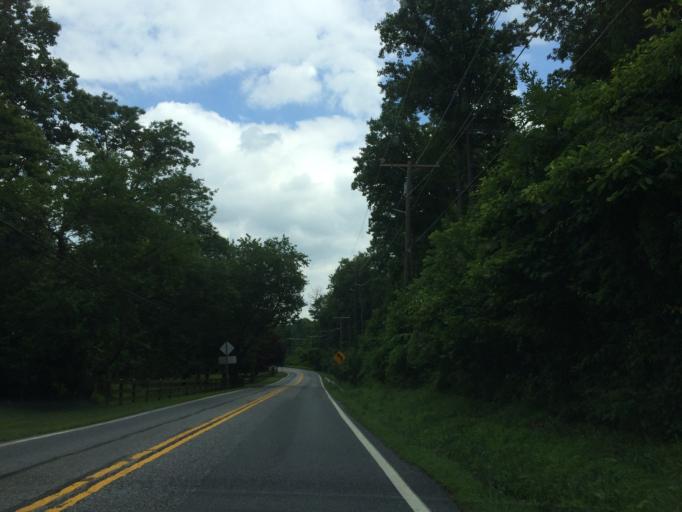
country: US
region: Maryland
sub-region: Baltimore County
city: Randallstown
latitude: 39.3437
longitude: -76.8250
